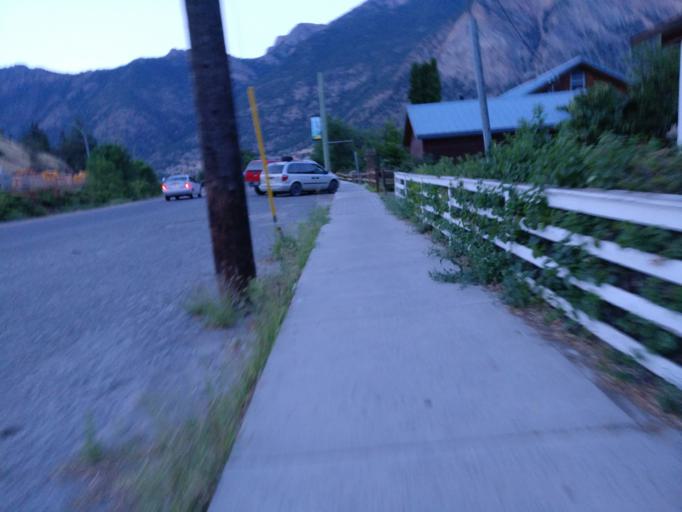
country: CA
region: British Columbia
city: Lillooet
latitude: 50.6961
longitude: -121.9292
